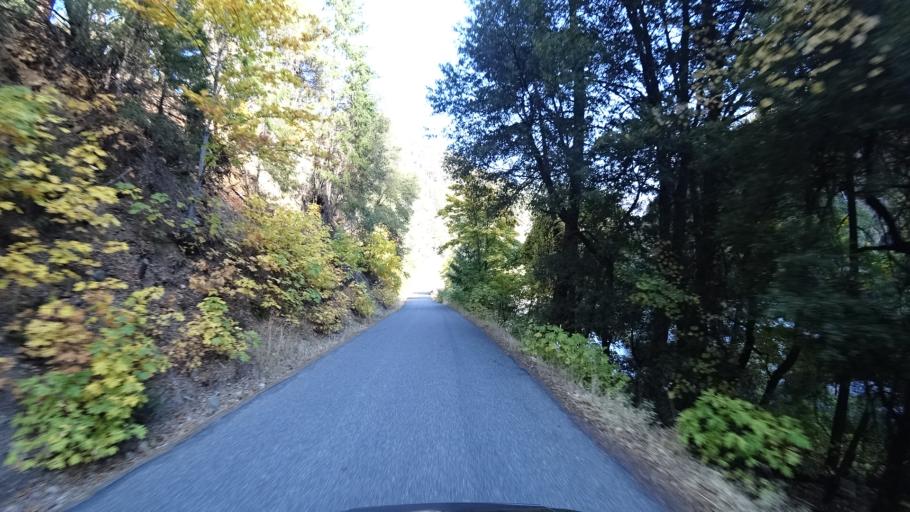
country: US
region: California
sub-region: Siskiyou County
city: Happy Camp
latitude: 41.6670
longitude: -123.1096
